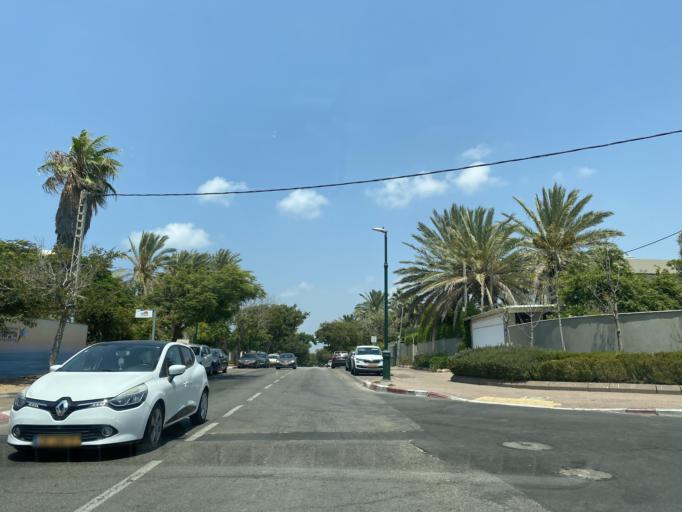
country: IL
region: Tel Aviv
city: Herzliya Pituah
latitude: 32.1765
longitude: 34.8048
